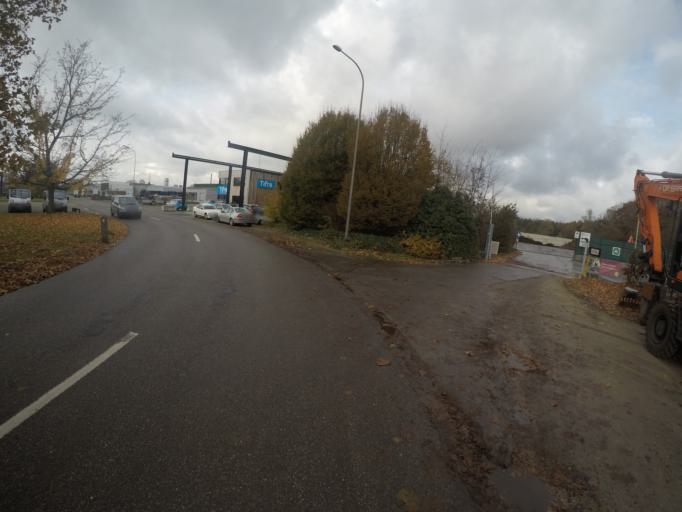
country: BE
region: Flanders
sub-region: Provincie Oost-Vlaanderen
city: Sint-Niklaas
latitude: 51.1430
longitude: 4.1551
